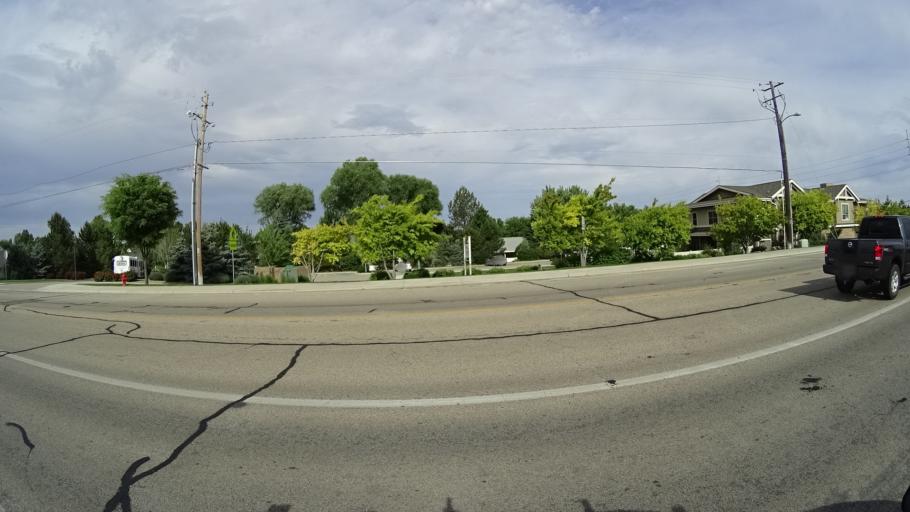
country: US
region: Idaho
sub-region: Ada County
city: Meridian
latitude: 43.5896
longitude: -116.3746
